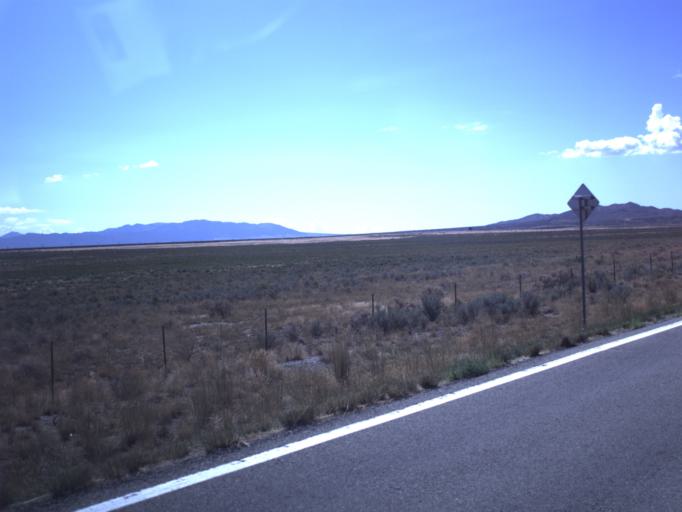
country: US
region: Utah
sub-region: Tooele County
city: Tooele
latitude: 40.2142
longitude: -112.4066
